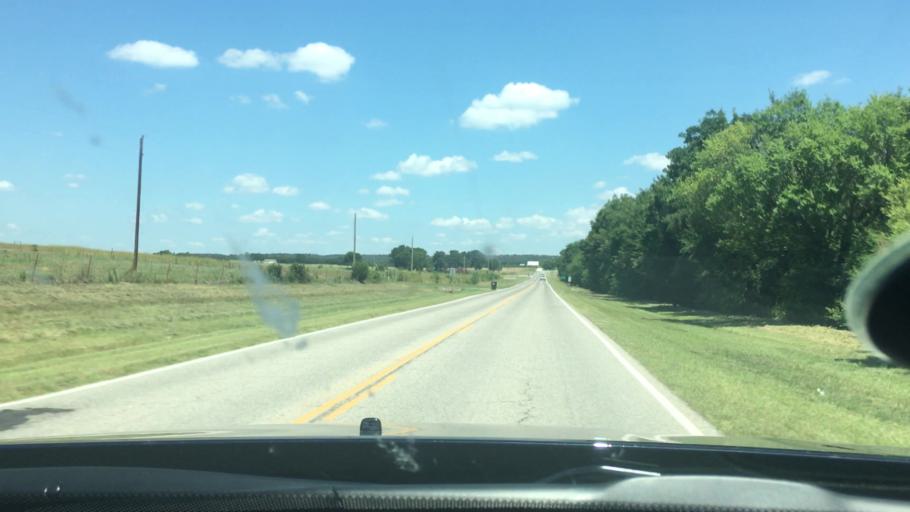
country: US
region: Oklahoma
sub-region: Carter County
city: Dickson
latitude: 34.2842
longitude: -96.9682
